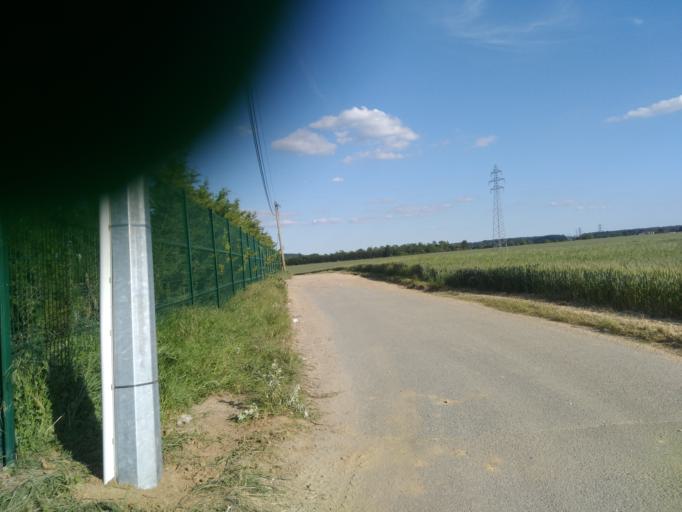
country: FR
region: Ile-de-France
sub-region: Departement des Yvelines
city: Thiverval-Grignon
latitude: 48.8318
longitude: 1.9301
